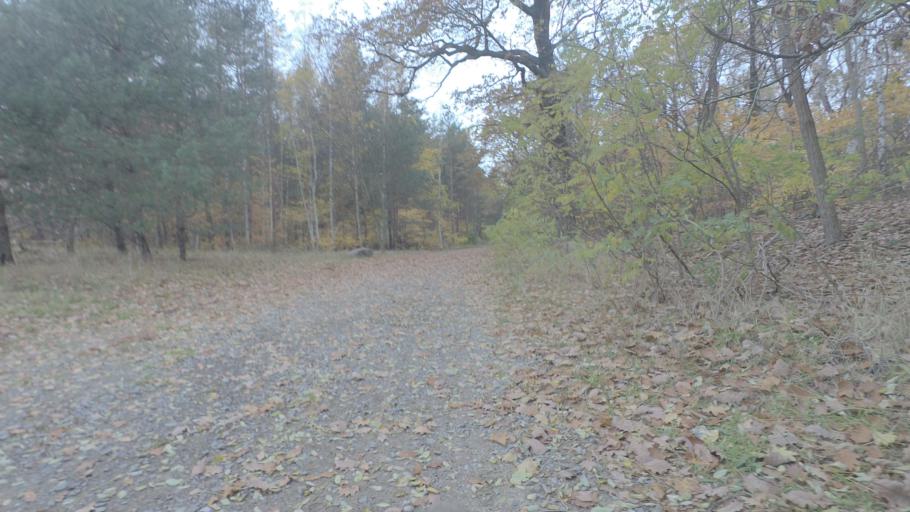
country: DE
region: Brandenburg
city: Rangsdorf
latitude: 52.3064
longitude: 13.4152
